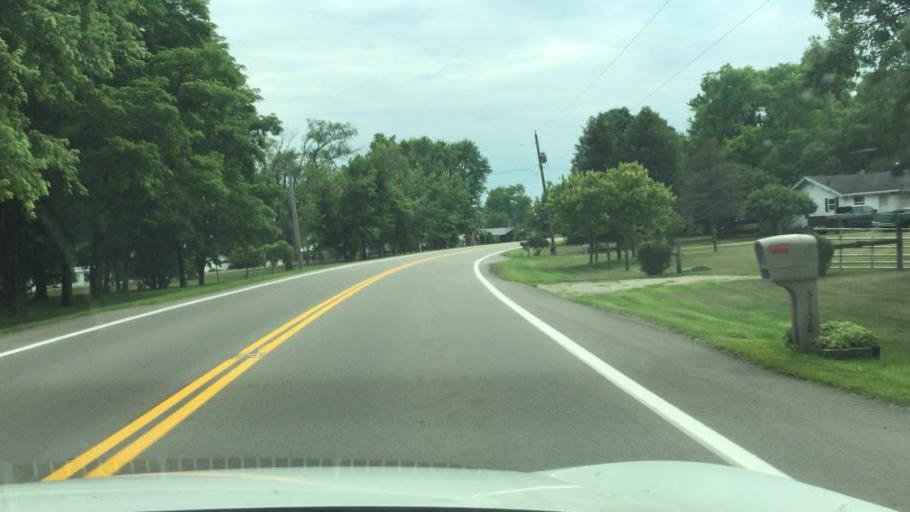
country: US
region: Ohio
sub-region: Champaign County
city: Mechanicsburg
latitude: 40.0237
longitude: -83.6593
